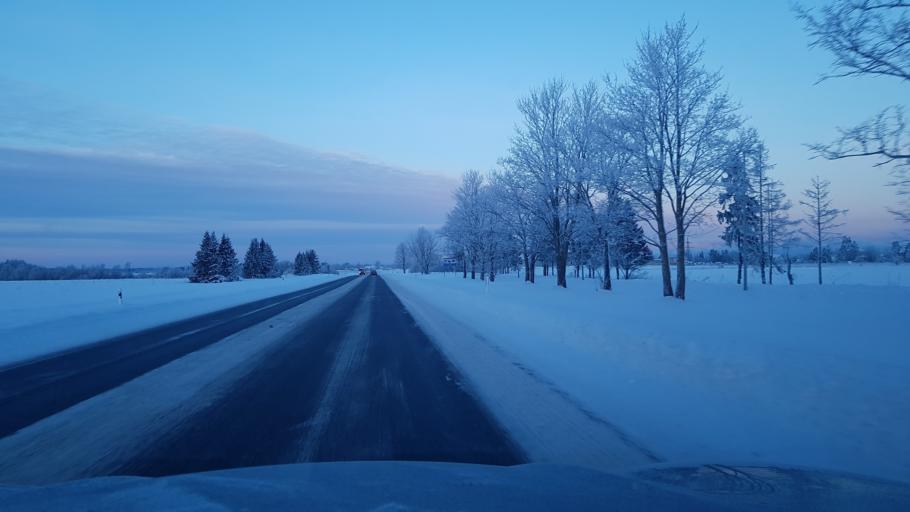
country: EE
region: Ida-Virumaa
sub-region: Narva linn
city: Narva
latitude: 59.3874
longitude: 28.1456
